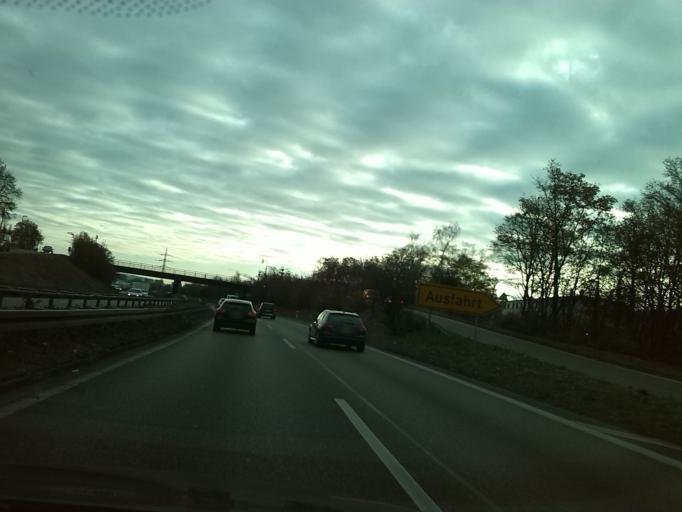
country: DE
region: Baden-Wuerttemberg
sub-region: Regierungsbezirk Stuttgart
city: Ostfildern
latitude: 48.7408
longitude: 9.2734
